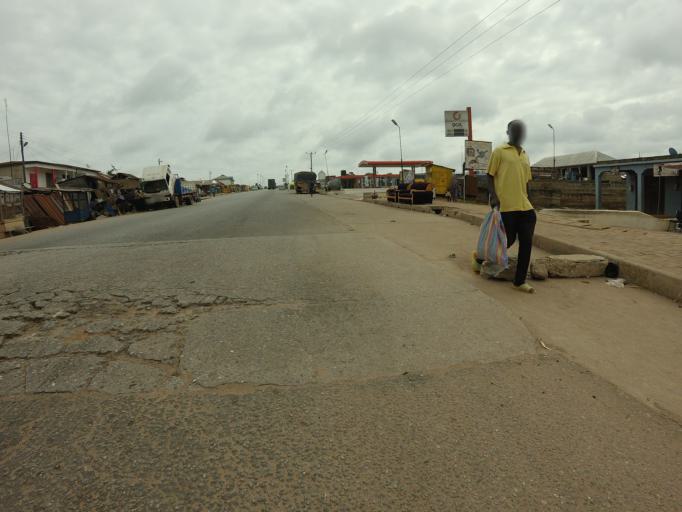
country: GH
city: Bechem
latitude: 7.1322
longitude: -1.7347
